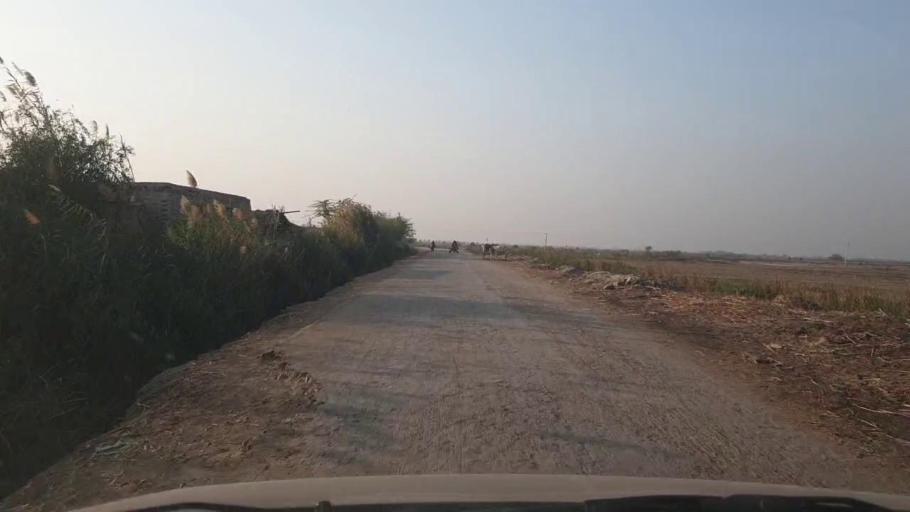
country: PK
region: Sindh
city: Mirwah Gorchani
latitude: 25.3737
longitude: 69.1255
